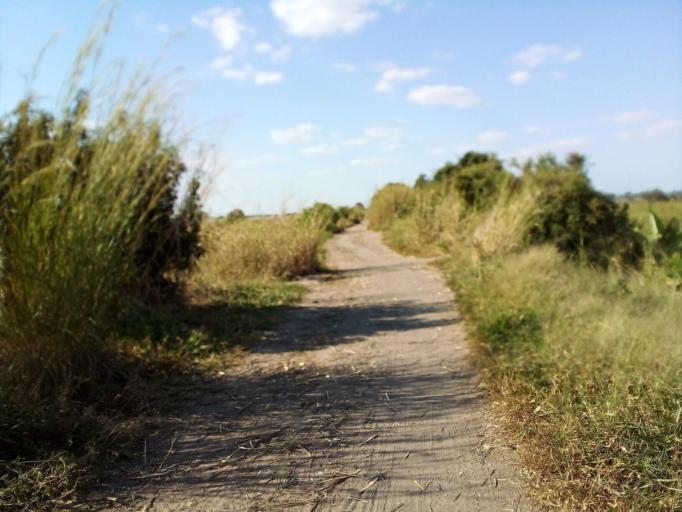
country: MZ
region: Zambezia
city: Quelimane
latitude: -17.5869
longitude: 36.8397
